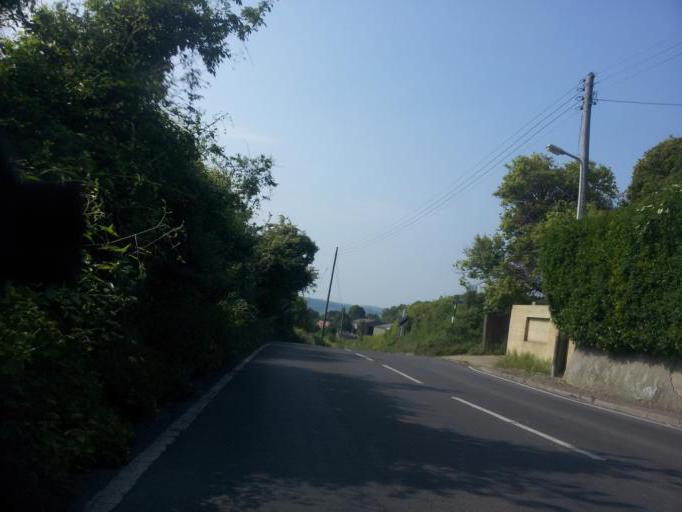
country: GB
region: England
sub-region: Kent
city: Snodland
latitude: 51.3375
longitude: 0.4733
